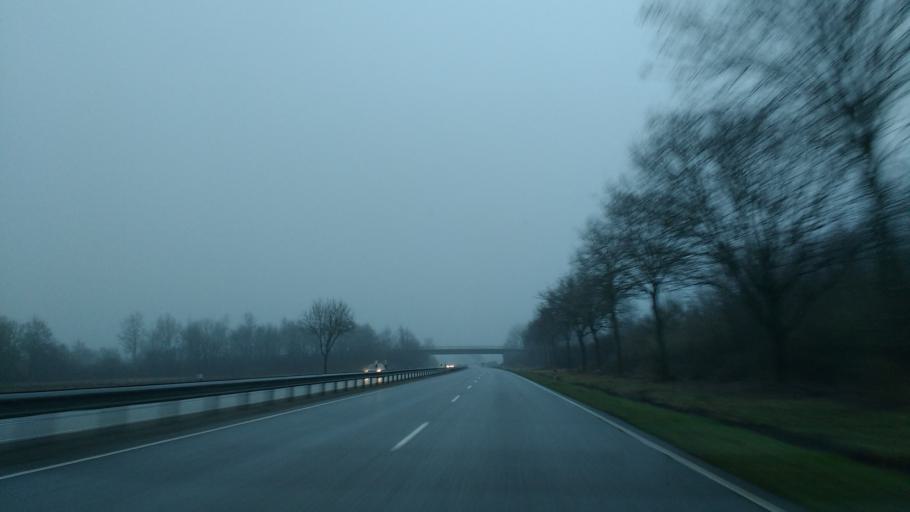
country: DE
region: Schleswig-Holstein
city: Jevenstedt
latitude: 54.2603
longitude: 9.6660
